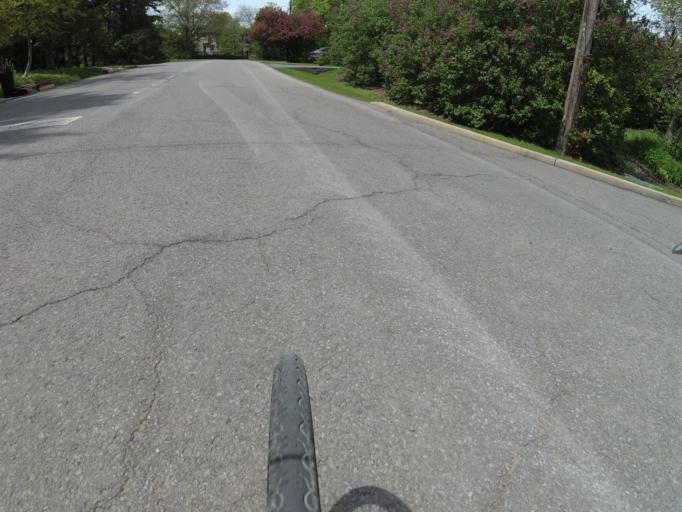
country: CA
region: Quebec
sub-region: Outaouais
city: Gatineau
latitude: 45.4518
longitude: -75.6080
